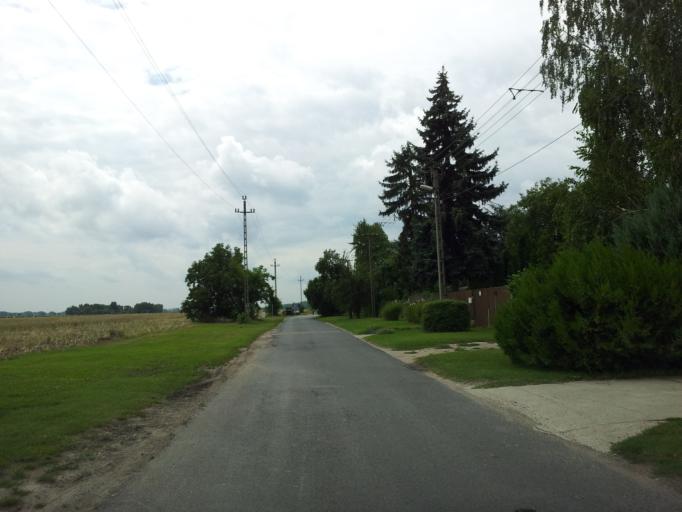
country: HU
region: Pest
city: Rackeve
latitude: 47.1904
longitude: 18.9597
